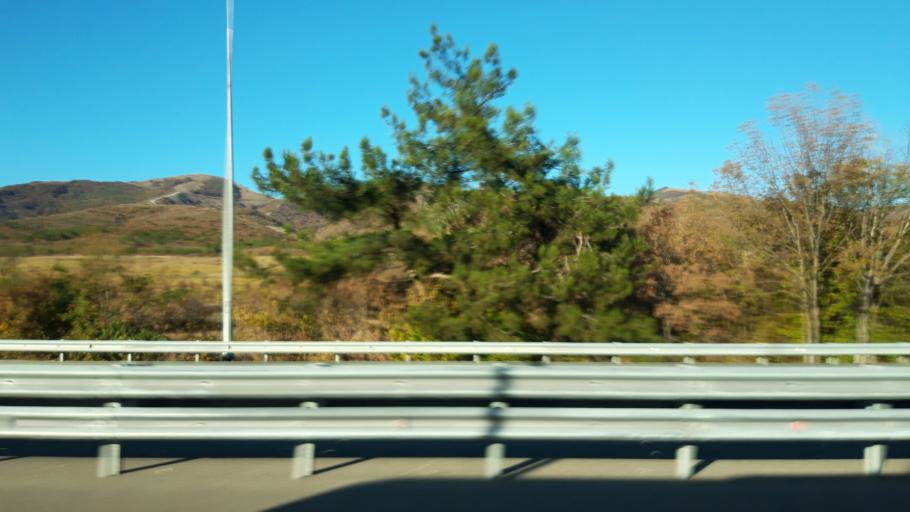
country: RU
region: Krasnodarskiy
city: Kabardinka
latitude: 44.6438
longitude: 37.9689
